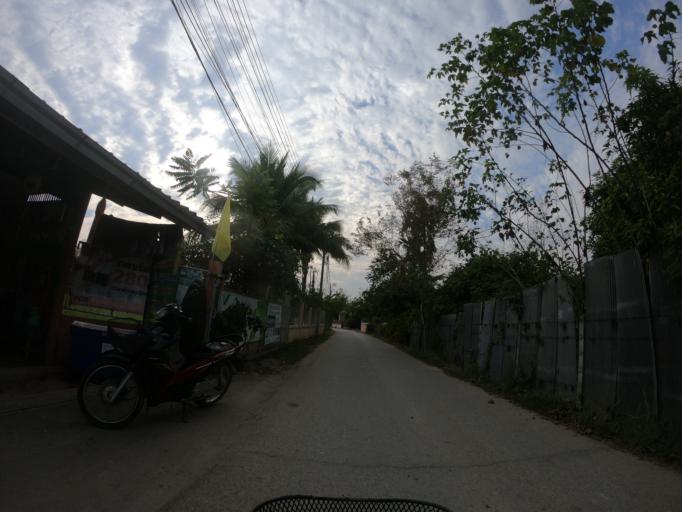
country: TH
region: Chiang Mai
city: San Sai
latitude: 18.8001
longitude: 99.0484
